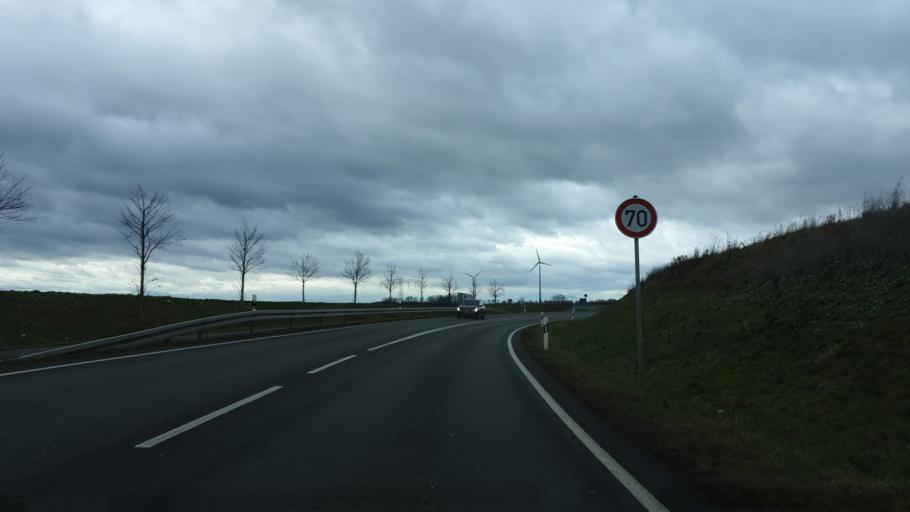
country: DE
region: Saxony
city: Callenberg
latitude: 50.8160
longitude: 12.6512
